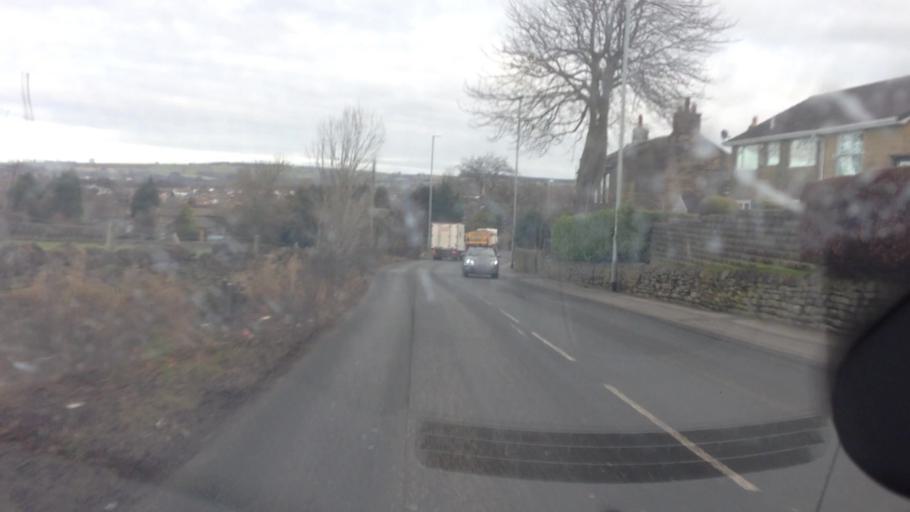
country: GB
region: England
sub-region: City and Borough of Leeds
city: Yeadon
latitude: 53.8551
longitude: -1.6919
